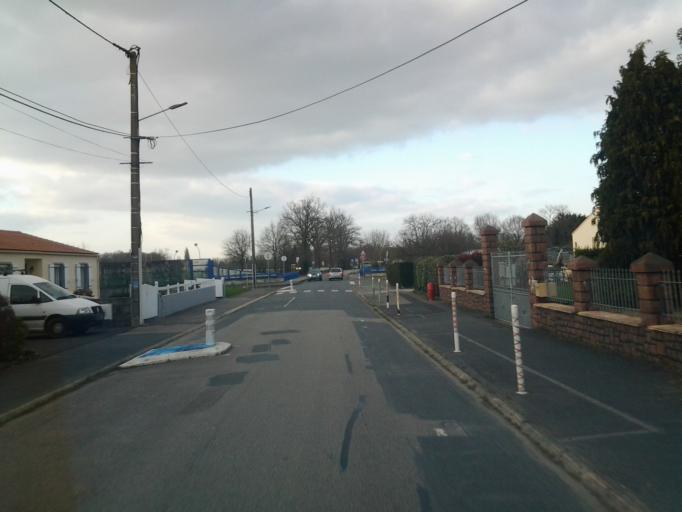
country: FR
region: Pays de la Loire
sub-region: Departement de la Vendee
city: La Roche-sur-Yon
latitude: 46.6870
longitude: -1.4406
